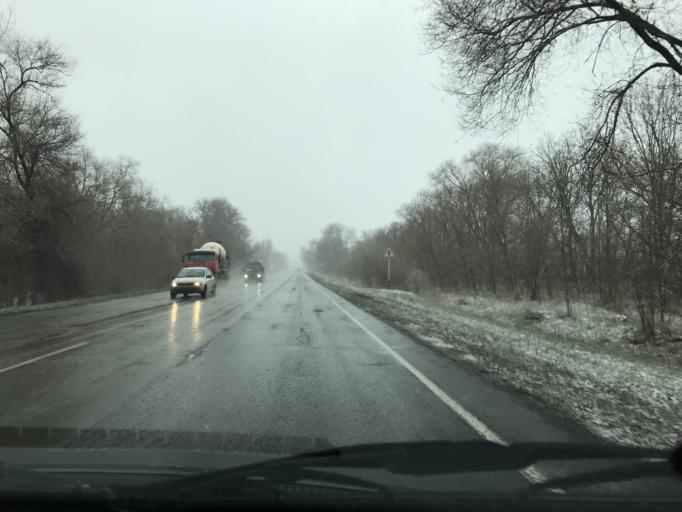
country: RU
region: Rostov
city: Kirovskaya
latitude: 47.0272
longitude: 39.8856
